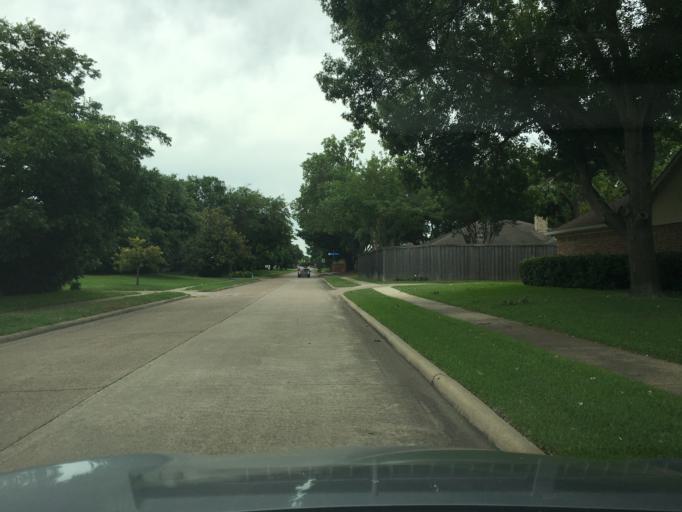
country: US
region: Texas
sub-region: Dallas County
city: Richardson
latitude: 32.9350
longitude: -96.7044
